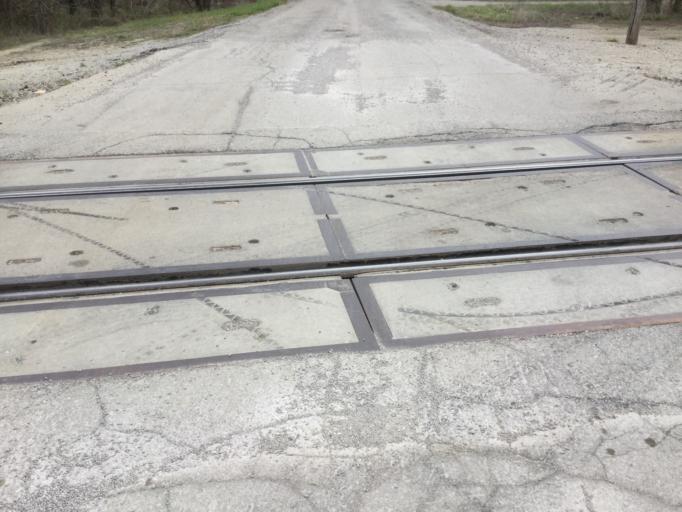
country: US
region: Kansas
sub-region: Bourbon County
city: Fort Scott
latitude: 37.7312
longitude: -94.6220
